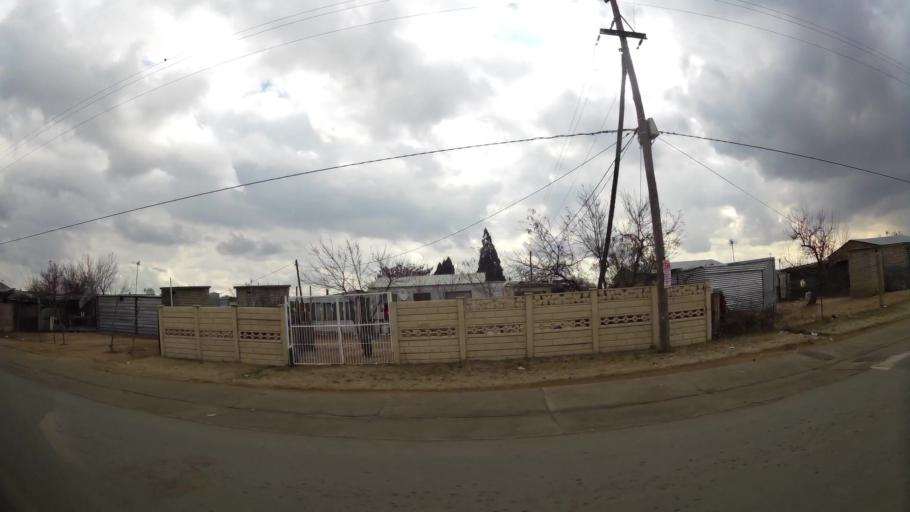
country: ZA
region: Orange Free State
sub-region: Fezile Dabi District Municipality
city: Sasolburg
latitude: -26.8528
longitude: 27.8737
